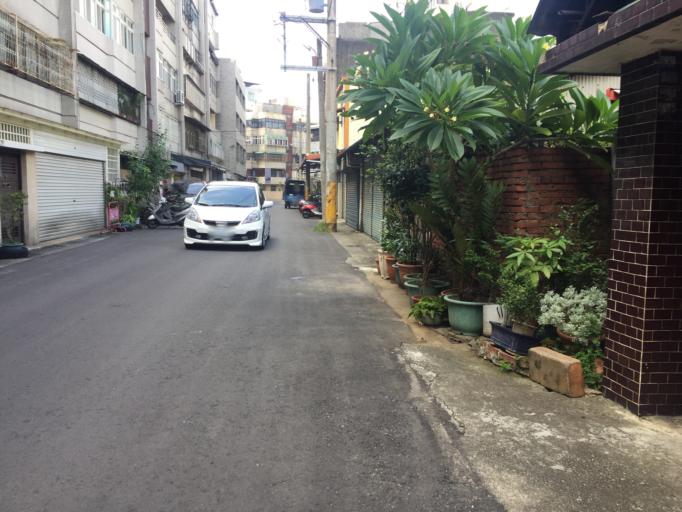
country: TW
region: Taiwan
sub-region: Hsinchu
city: Hsinchu
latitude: 24.7960
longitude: 120.9779
